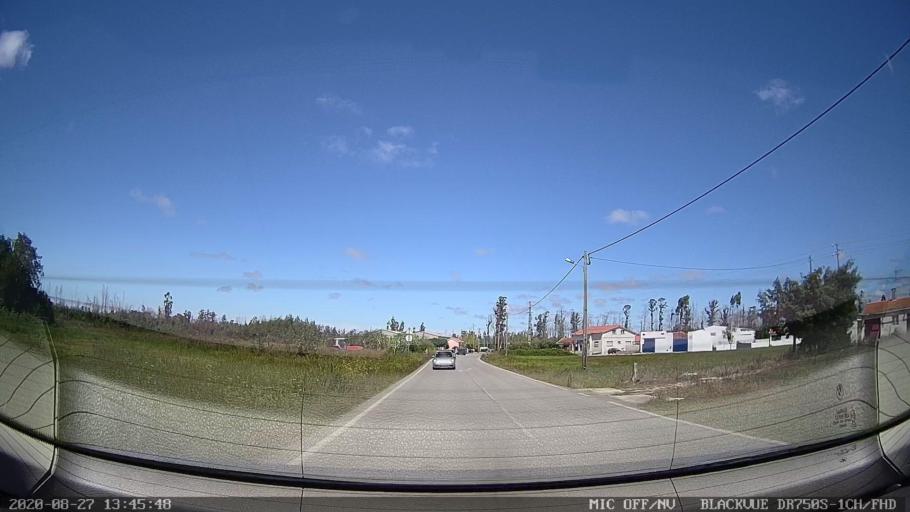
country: PT
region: Coimbra
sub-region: Mira
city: Mira
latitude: 40.4016
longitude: -8.7354
